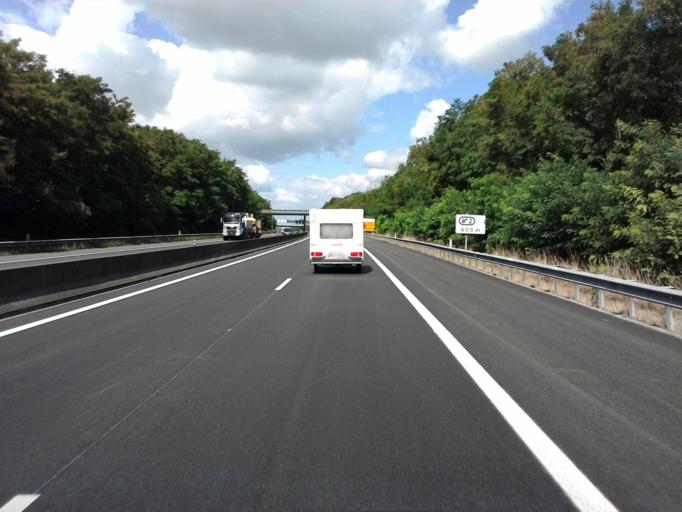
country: LU
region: Luxembourg
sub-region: Canton de Capellen
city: Mamer
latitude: 49.6372
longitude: 6.0233
